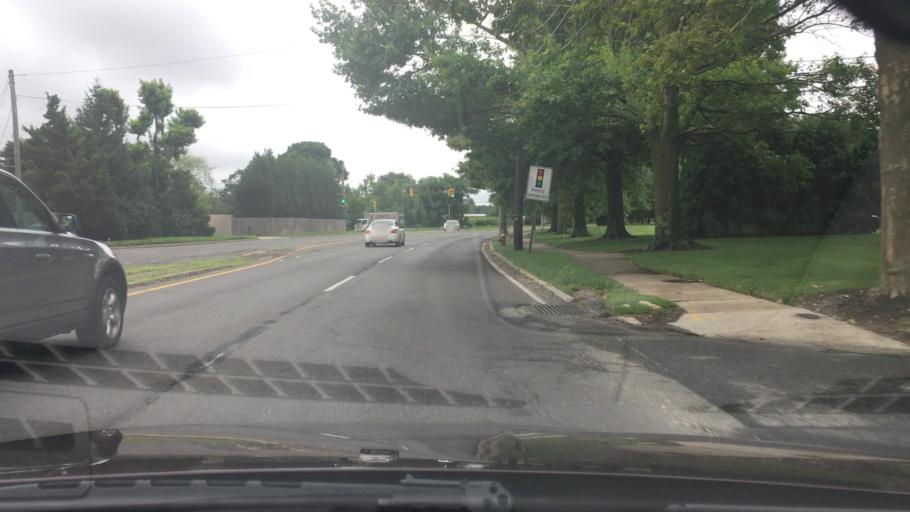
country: US
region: New York
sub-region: Suffolk County
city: Melville
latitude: 40.7791
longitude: -73.4057
